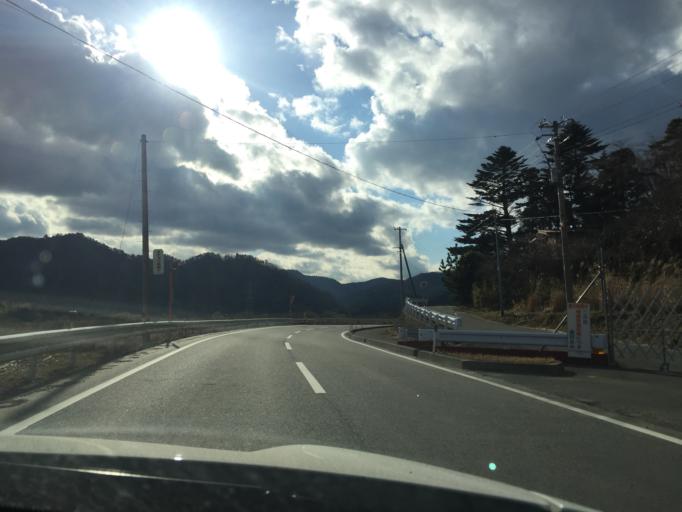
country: JP
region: Fukushima
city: Namie
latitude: 37.4128
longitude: 140.9589
